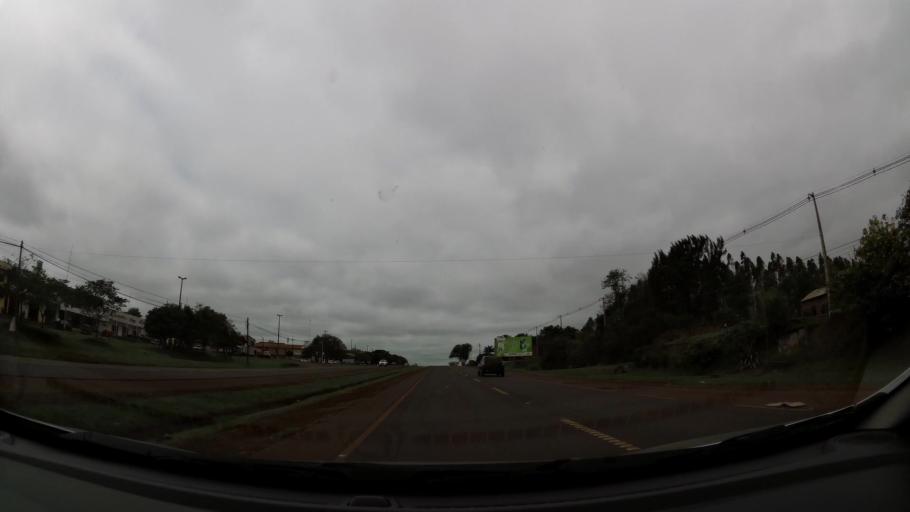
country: PY
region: Alto Parana
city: Presidente Franco
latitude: -25.4907
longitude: -54.7687
